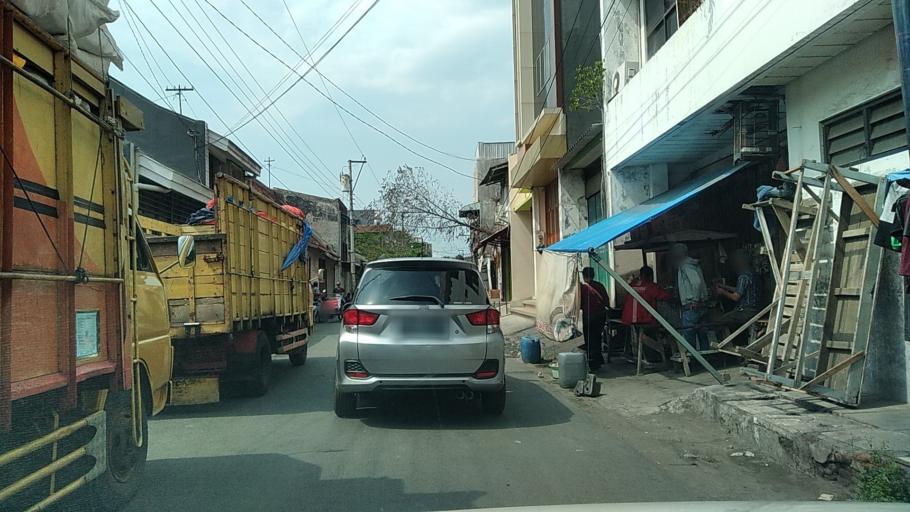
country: ID
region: Central Java
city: Semarang
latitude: -6.9775
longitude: 110.4260
